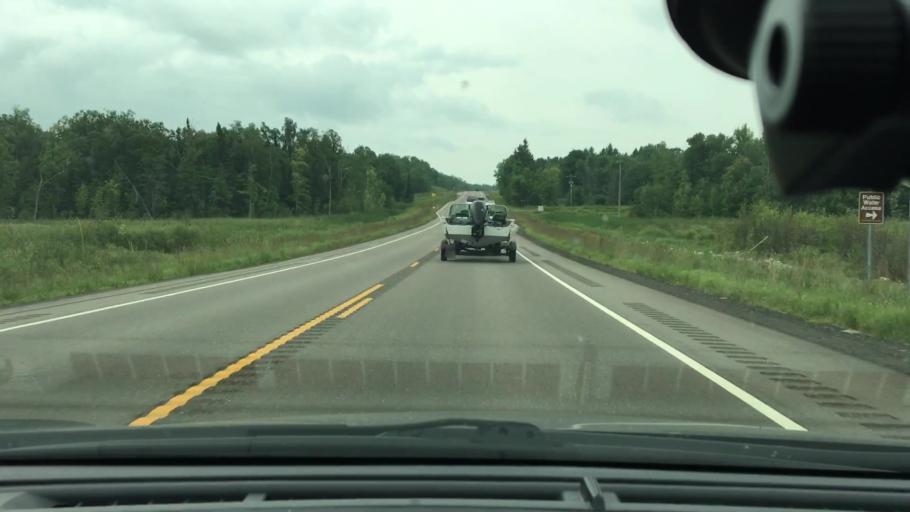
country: US
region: Minnesota
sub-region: Crow Wing County
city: Crosby
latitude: 46.6164
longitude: -93.9477
